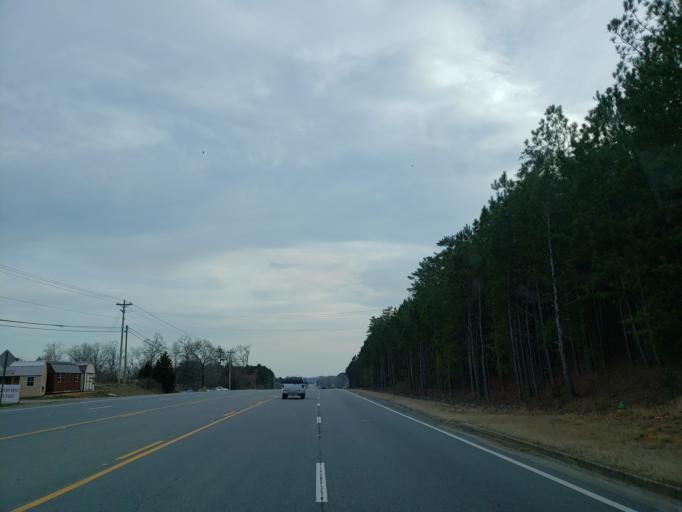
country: US
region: Georgia
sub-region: Whitfield County
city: Varnell
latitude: 34.9177
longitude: -84.9456
